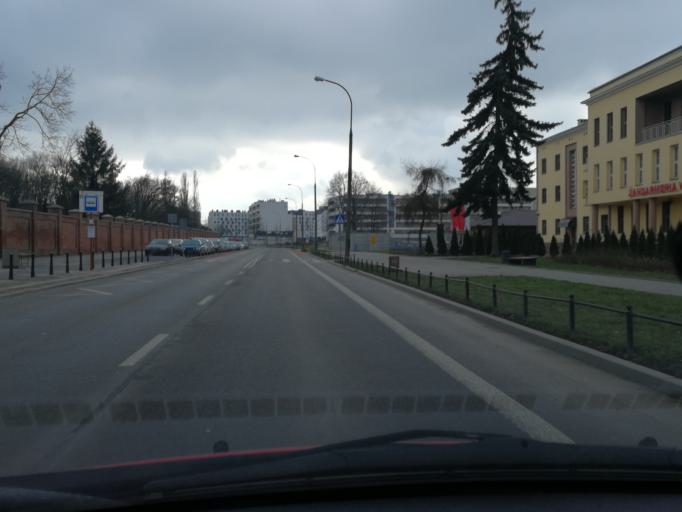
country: PL
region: Masovian Voivodeship
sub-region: Warszawa
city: Wola
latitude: 52.2496
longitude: 20.9651
